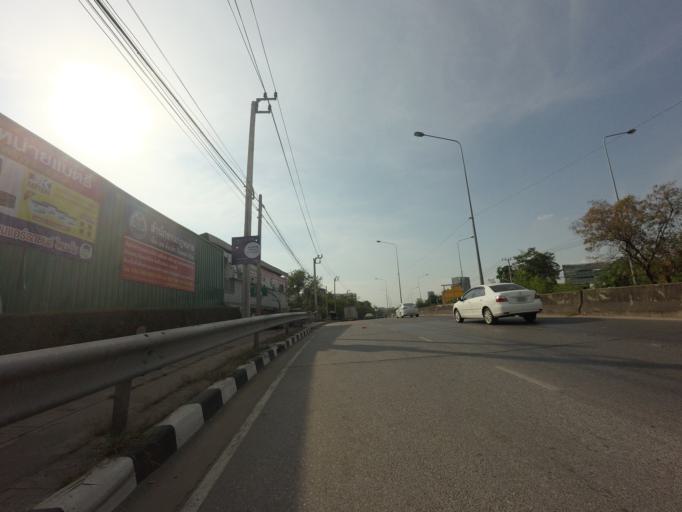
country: TH
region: Bangkok
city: Bang Kapi
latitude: 13.7524
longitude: 100.6331
